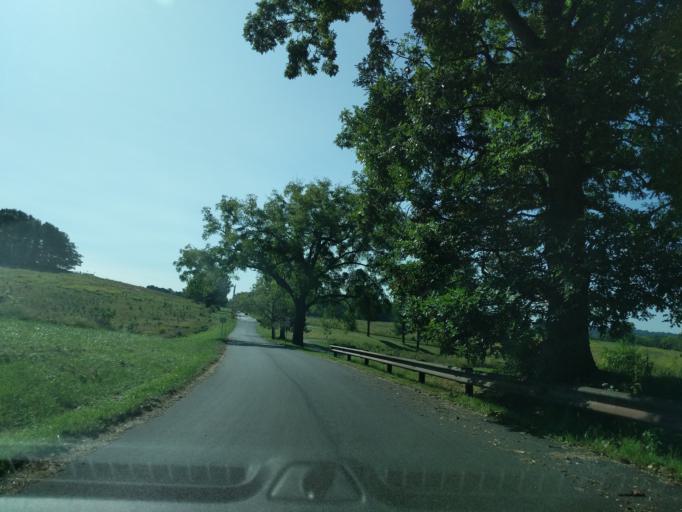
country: US
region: Pennsylvania
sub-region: Chester County
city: Chesterbrook
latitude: 40.0890
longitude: -75.4498
